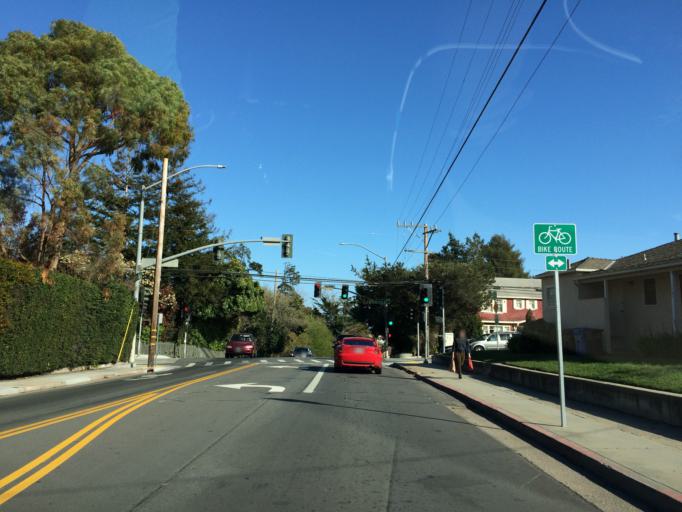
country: US
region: California
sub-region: Santa Cruz County
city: Santa Cruz
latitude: 36.9690
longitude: -122.0354
